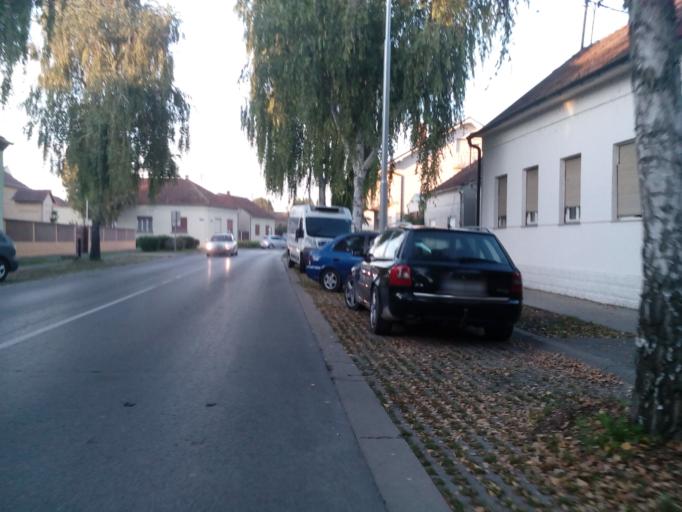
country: HR
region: Vukovarsko-Srijemska
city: Vinkovci
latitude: 45.2925
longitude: 18.8115
